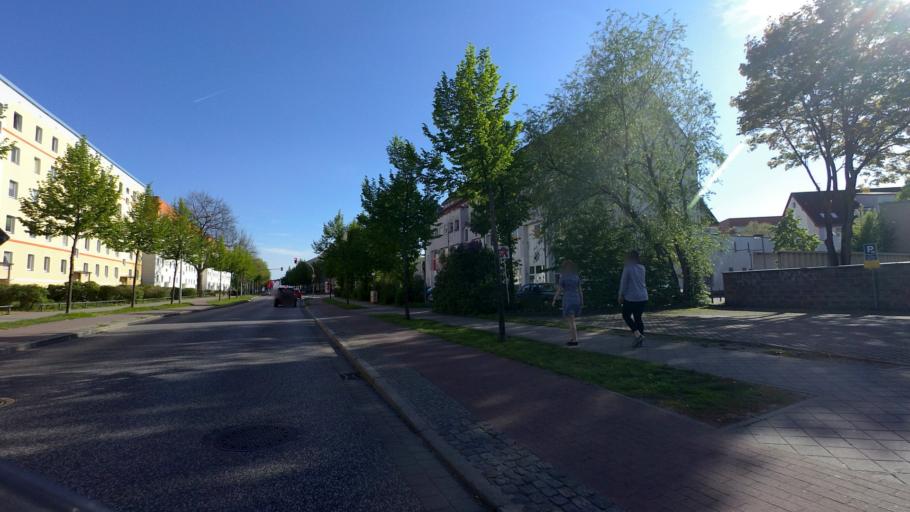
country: DE
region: Brandenburg
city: Oranienburg
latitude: 52.7474
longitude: 13.2373
